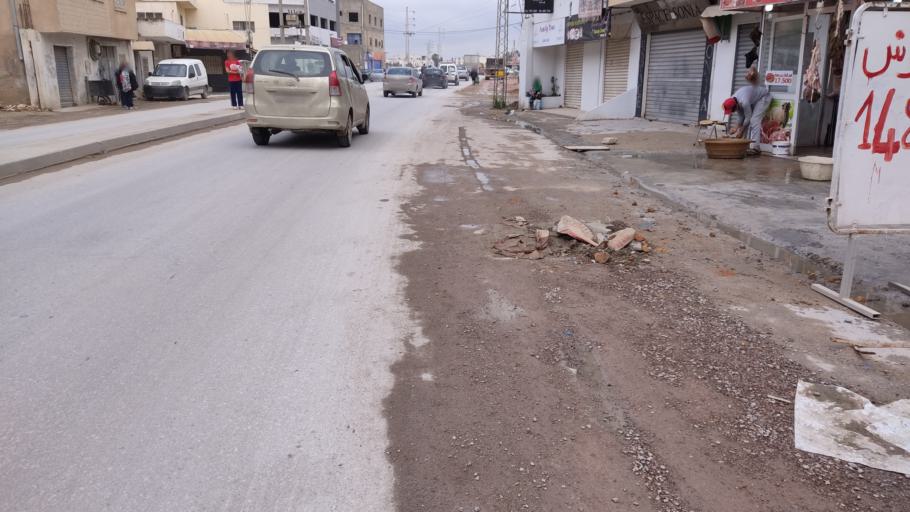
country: TN
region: Ariana
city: Ariana
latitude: 36.8900
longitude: 10.2131
